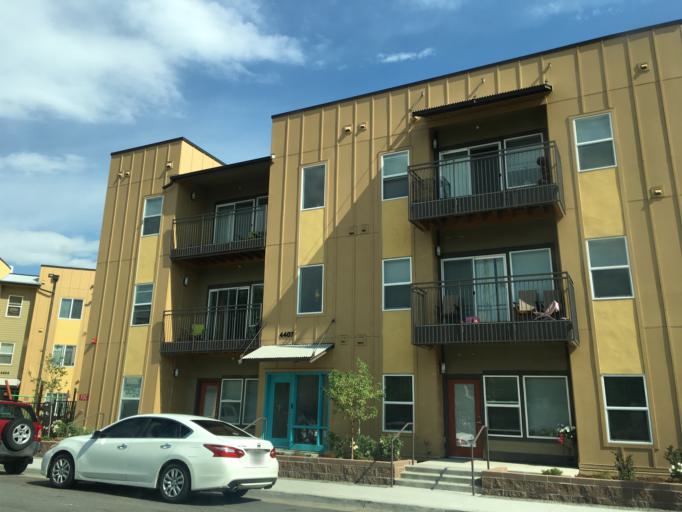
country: US
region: Colorado
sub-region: Jefferson County
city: Lakewood
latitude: 39.7021
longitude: -105.0444
